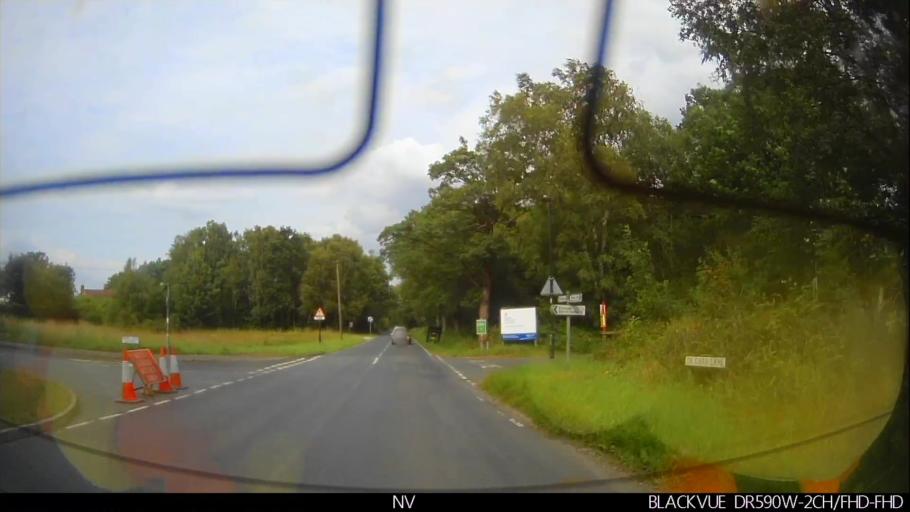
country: GB
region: England
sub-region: North Yorkshire
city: Strensall
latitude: 54.0319
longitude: -1.0319
